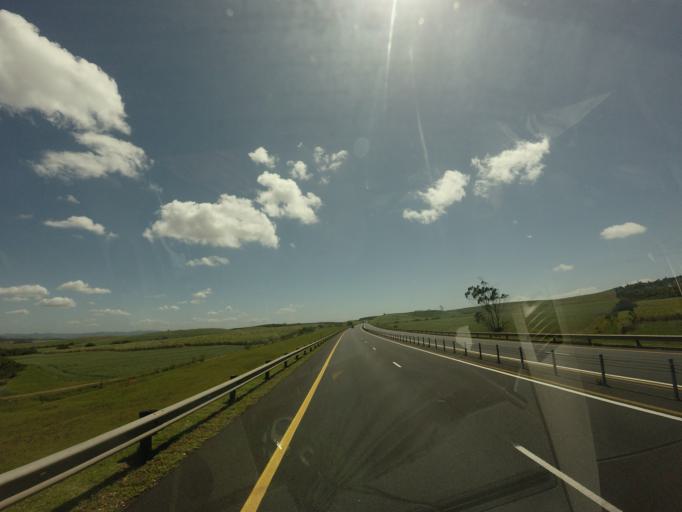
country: ZA
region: KwaZulu-Natal
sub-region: uThungulu District Municipality
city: Eshowe
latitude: -29.0547
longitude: 31.6323
